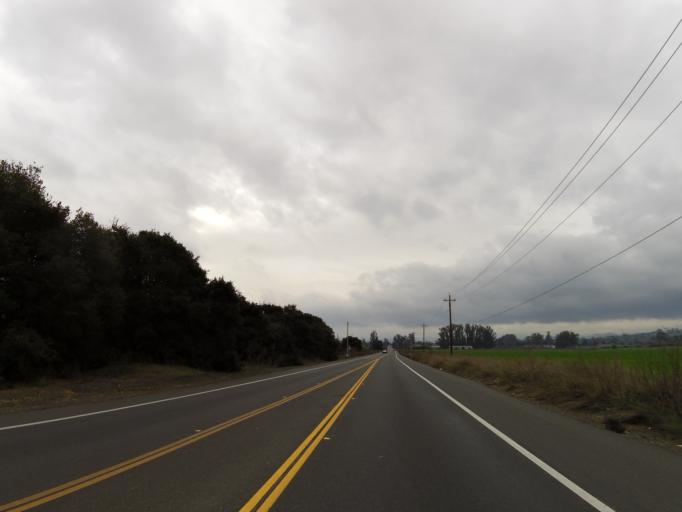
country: US
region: California
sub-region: Sonoma County
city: Penngrove
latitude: 38.3208
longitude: -122.6669
